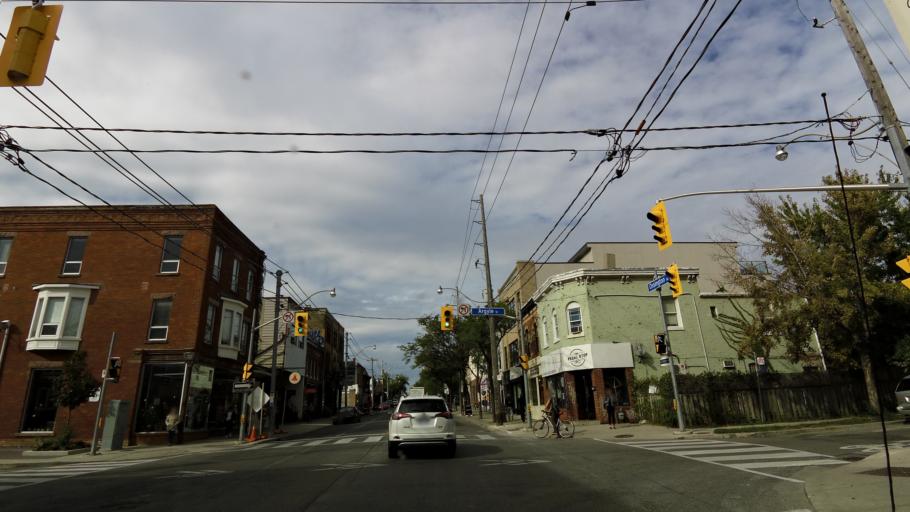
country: CA
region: Ontario
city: Toronto
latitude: 43.6467
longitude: -79.4199
